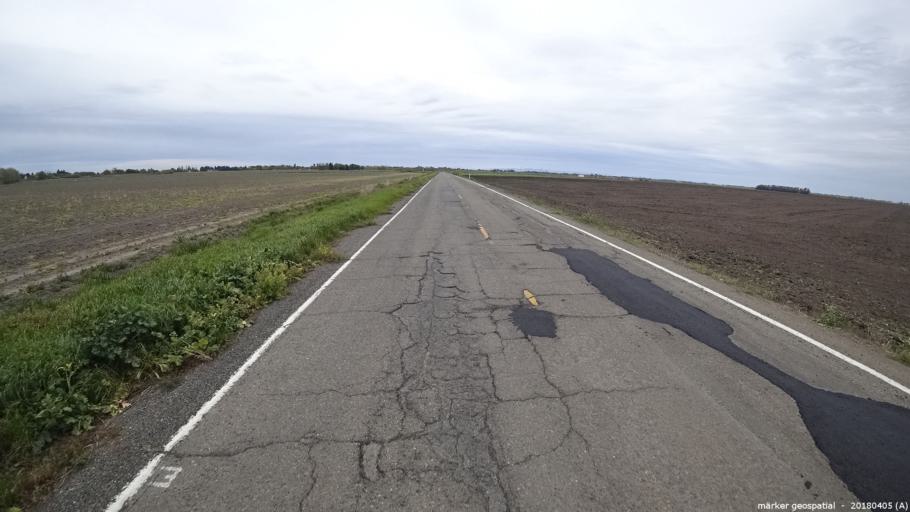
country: US
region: California
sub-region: Sacramento County
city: Walnut Grove
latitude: 38.2843
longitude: -121.5210
